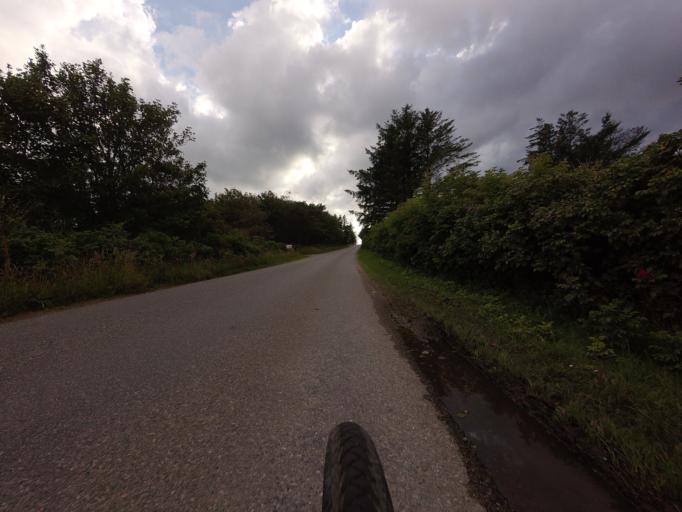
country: DK
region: North Denmark
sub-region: Hjorring Kommune
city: Hjorring
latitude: 57.4749
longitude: 9.8164
